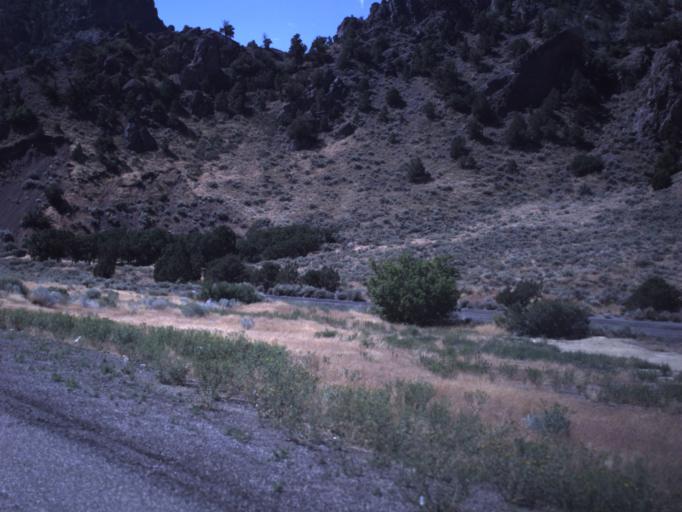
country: US
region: Utah
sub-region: Sevier County
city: Monroe
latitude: 38.5406
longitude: -112.2683
